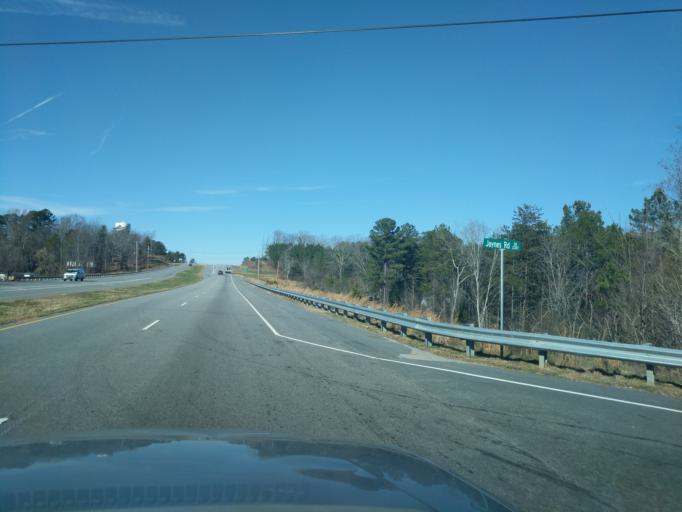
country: US
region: North Carolina
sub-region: Rutherford County
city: Forest City
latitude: 35.2535
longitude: -81.8763
